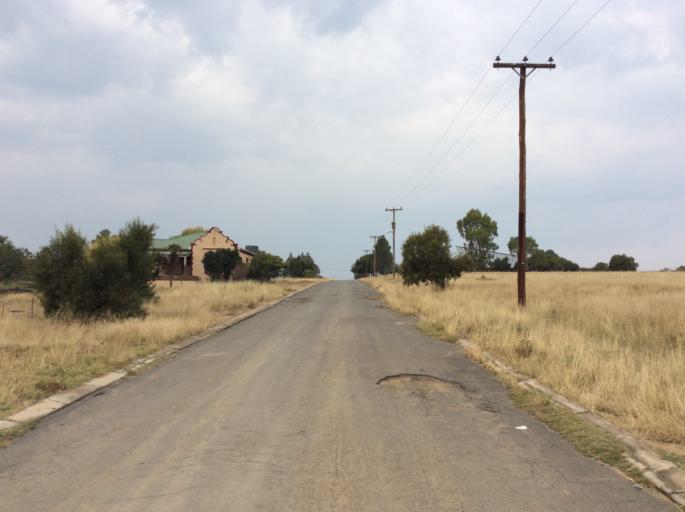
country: LS
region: Mafeteng
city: Mafeteng
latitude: -29.9872
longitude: 27.0092
